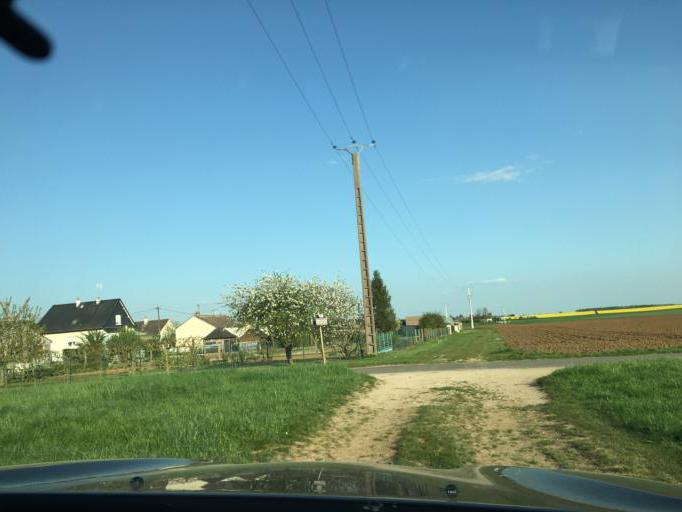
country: FR
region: Centre
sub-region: Departement du Loiret
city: Epieds-en-Beauce
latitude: 47.9257
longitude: 1.5816
